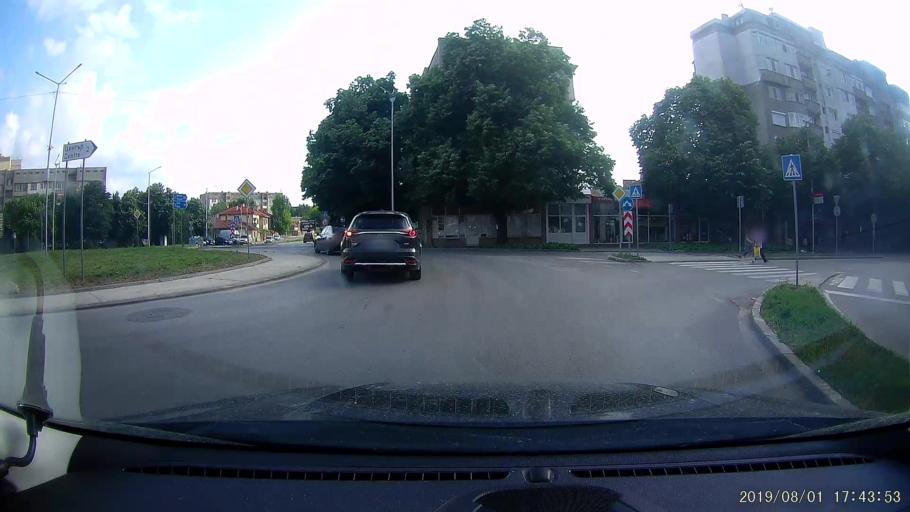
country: BG
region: Silistra
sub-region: Obshtina Silistra
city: Silistra
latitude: 44.1122
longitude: 27.2723
